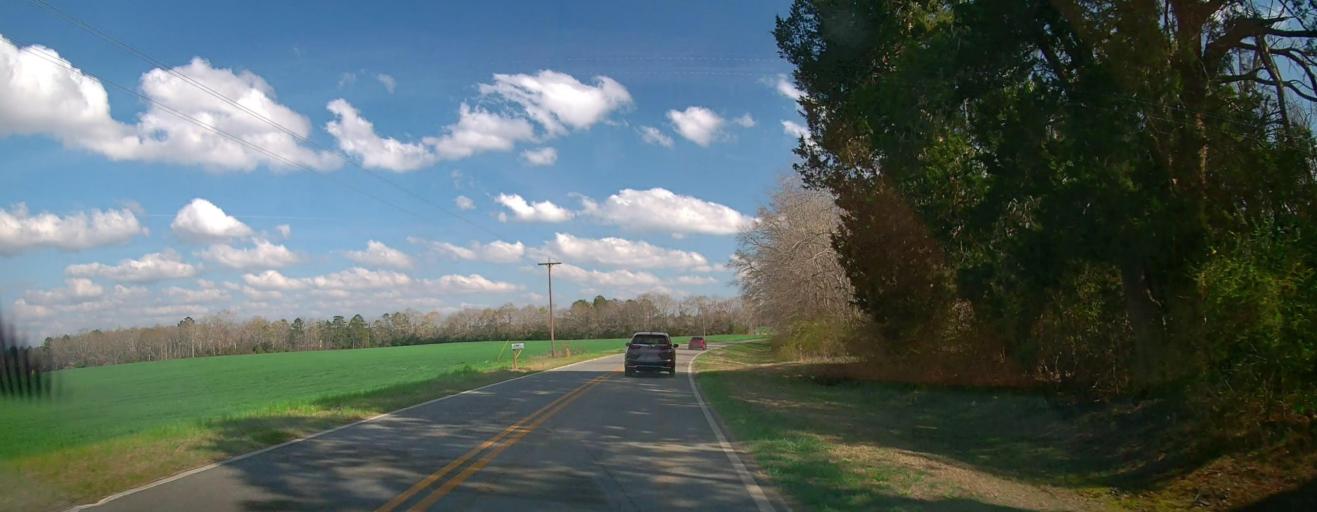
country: US
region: Georgia
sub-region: Wilkinson County
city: Irwinton
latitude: 32.6325
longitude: -83.1037
